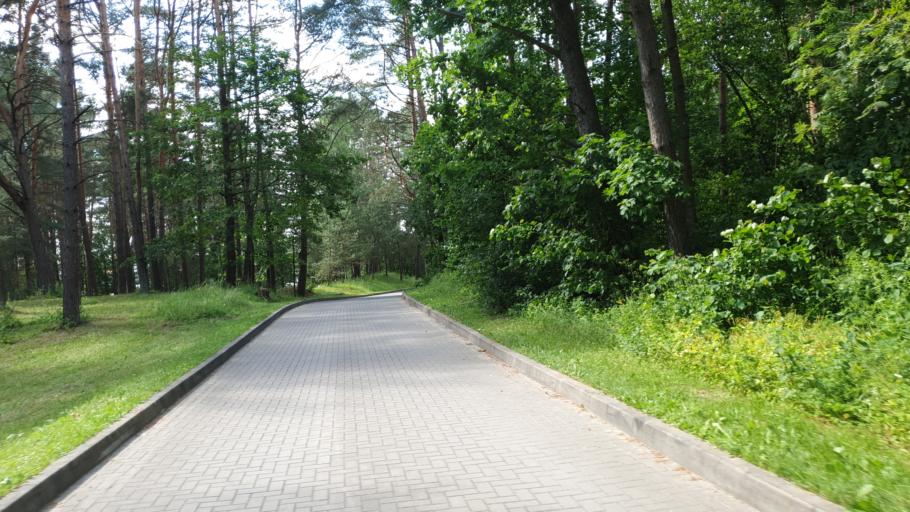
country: LT
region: Vilnius County
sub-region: Vilnius
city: Fabijoniskes
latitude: 54.7934
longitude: 25.3002
